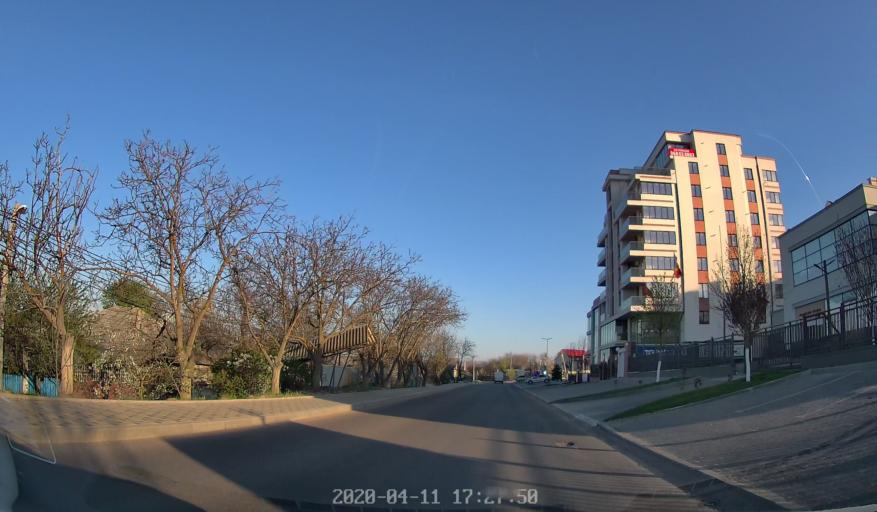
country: MD
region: Laloveni
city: Ialoveni
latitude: 47.0078
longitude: 28.7637
